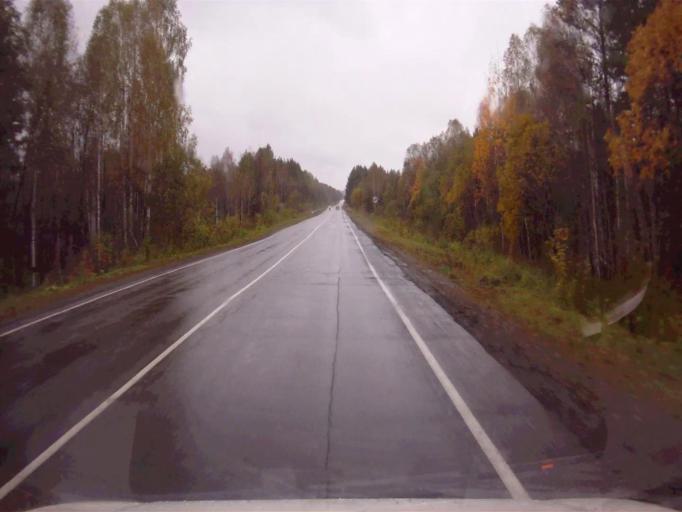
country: RU
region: Chelyabinsk
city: Verkhniy Ufaley
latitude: 55.9721
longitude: 60.3562
